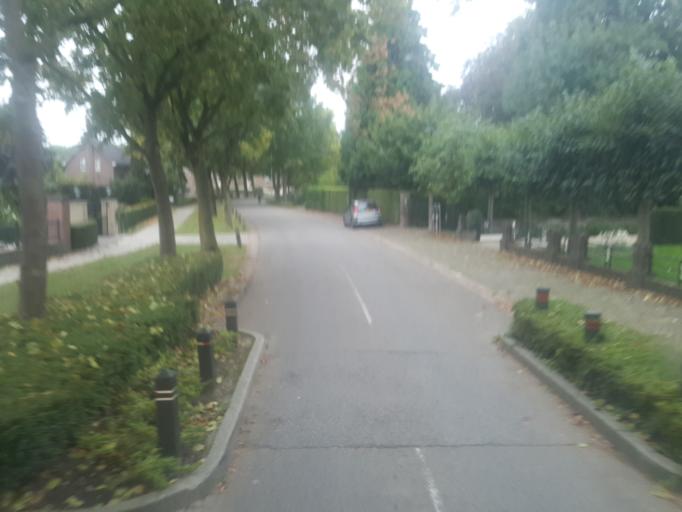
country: NL
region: Gelderland
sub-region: Gemeente Tiel
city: Tiel
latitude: 51.8469
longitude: 5.4286
